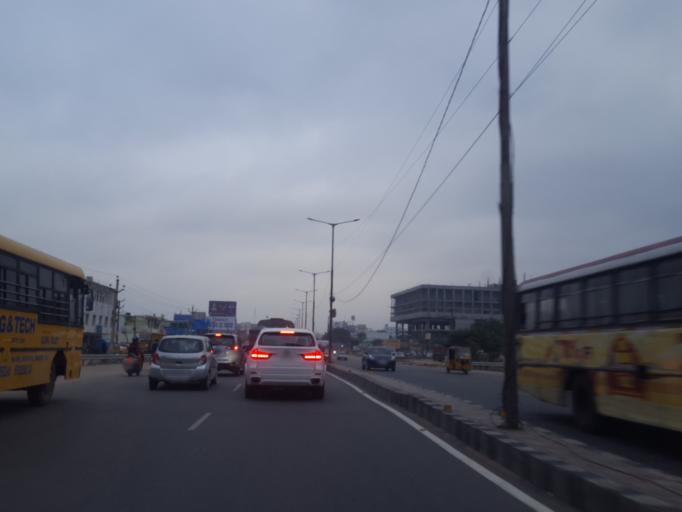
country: IN
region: Telangana
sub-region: Medak
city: Serilingampalle
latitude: 17.5120
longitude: 78.2932
